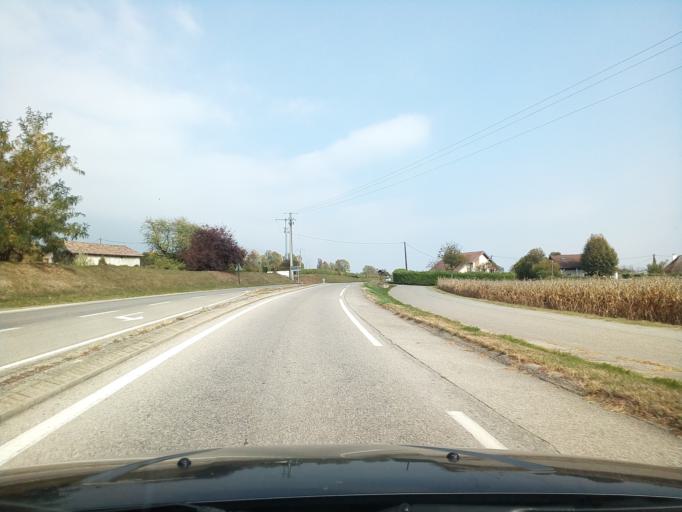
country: FR
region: Rhone-Alpes
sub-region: Departement de l'Isere
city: Saint-Ismier
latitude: 45.2326
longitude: 5.8235
